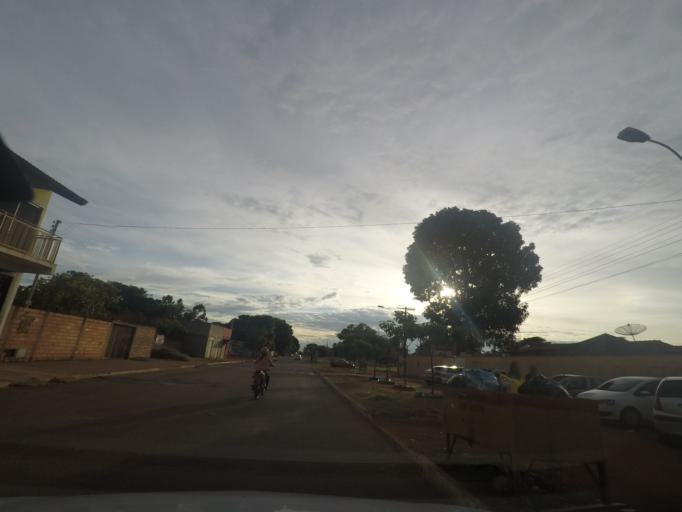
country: BR
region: Goias
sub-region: Trindade
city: Trindade
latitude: -16.7203
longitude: -49.4346
